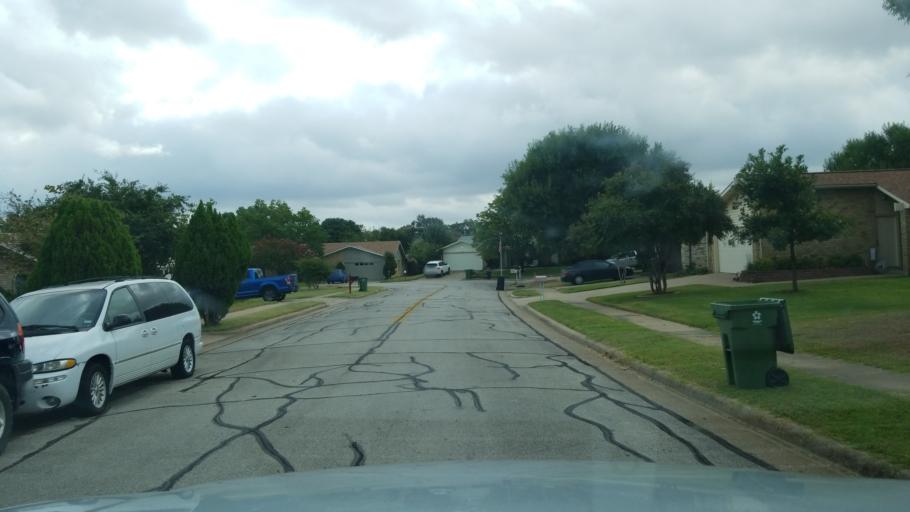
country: US
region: Texas
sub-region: Tarrant County
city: Euless
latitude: 32.8459
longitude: -97.1053
